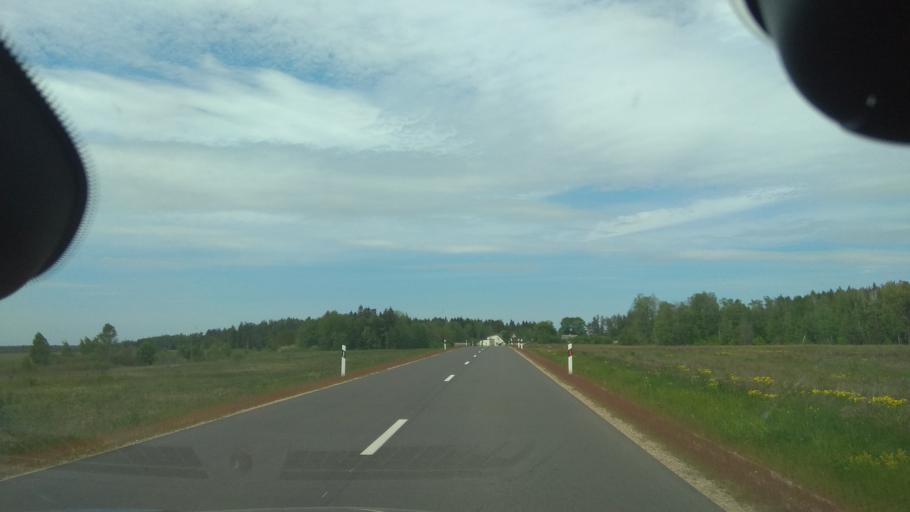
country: LT
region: Vilnius County
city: Ukmerge
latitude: 55.1273
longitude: 24.6032
